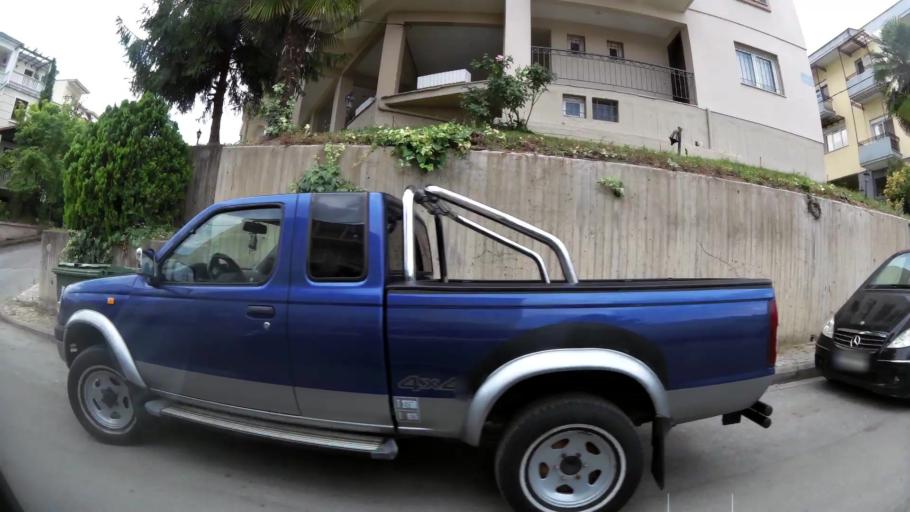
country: GR
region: Central Macedonia
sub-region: Nomos Imathias
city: Veroia
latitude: 40.5214
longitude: 22.2095
